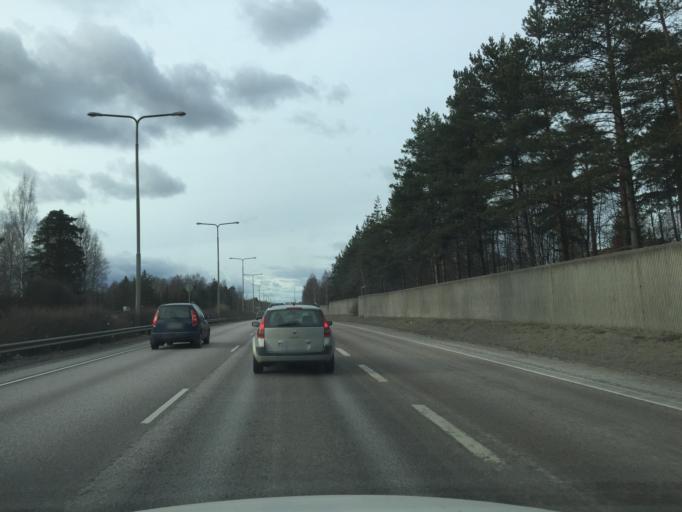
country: FI
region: Uusimaa
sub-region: Helsinki
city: Teekkarikylae
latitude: 60.2433
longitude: 24.8927
